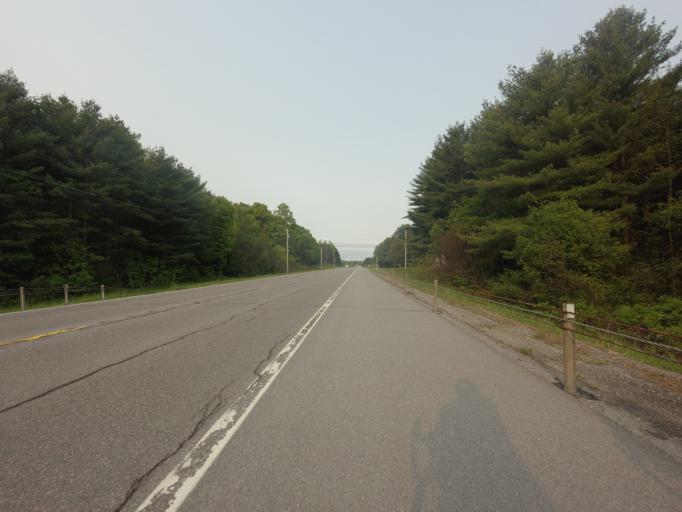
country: US
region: New York
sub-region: Jefferson County
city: Carthage
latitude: 44.0731
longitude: -75.4776
